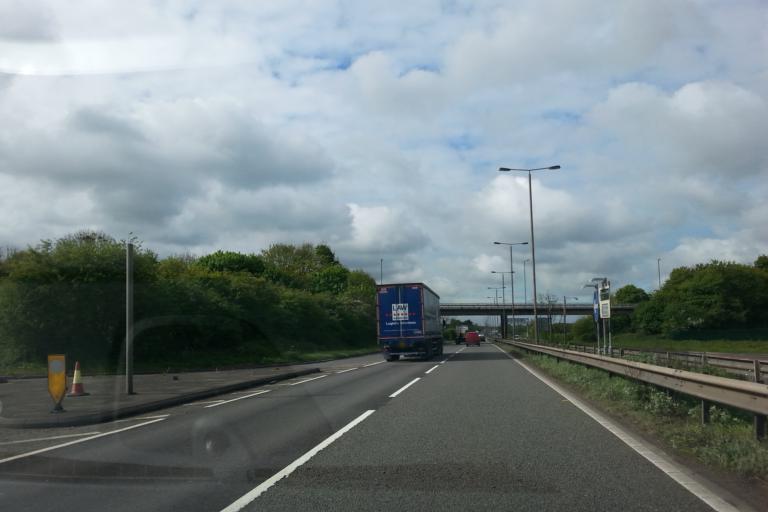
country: GB
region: England
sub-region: Derbyshire
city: Etwall
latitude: 52.8547
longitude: -1.5825
